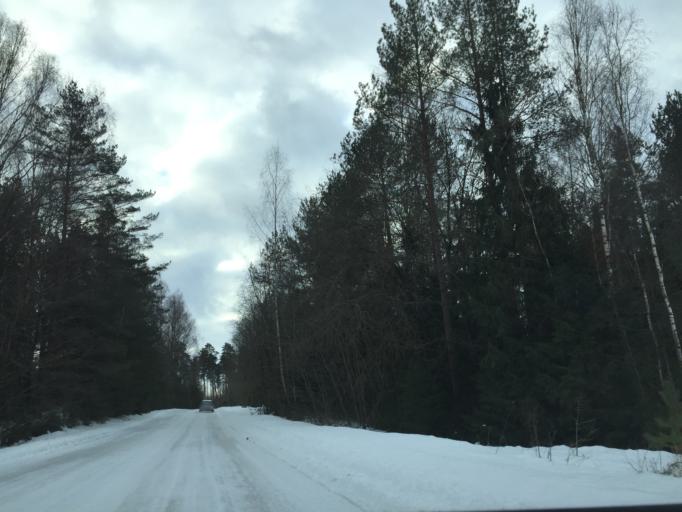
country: LV
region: Lielvarde
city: Lielvarde
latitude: 56.6216
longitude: 24.7750
